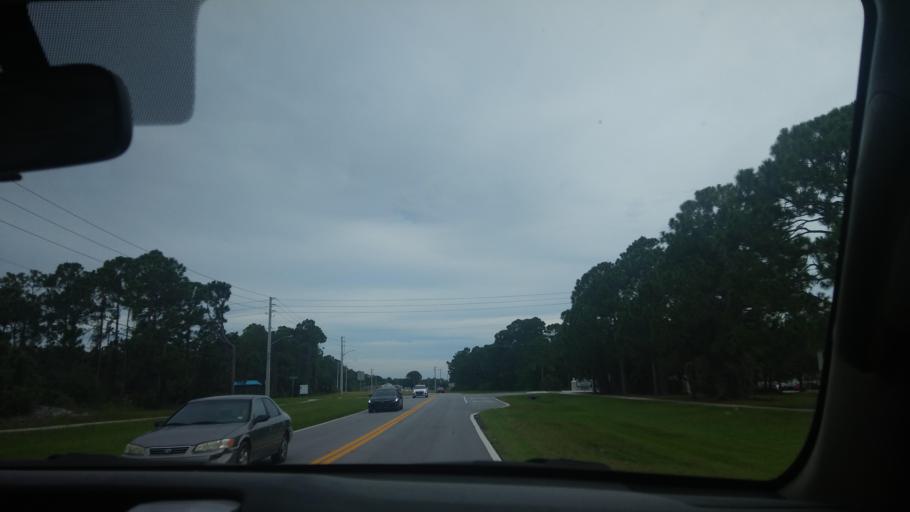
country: US
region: Florida
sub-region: Brevard County
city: Palm Bay
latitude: 27.9848
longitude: -80.6349
